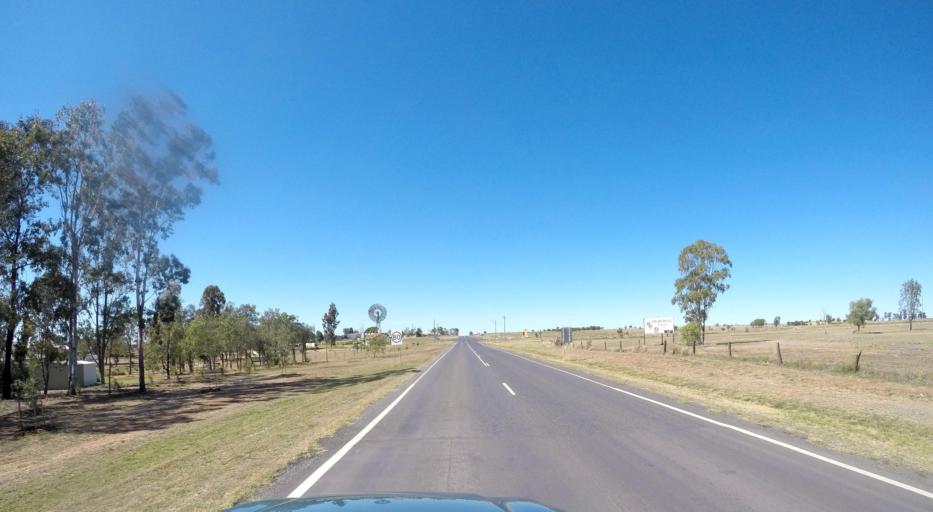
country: AU
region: Queensland
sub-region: Banana
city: Taroom
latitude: -26.1208
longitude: 149.9566
